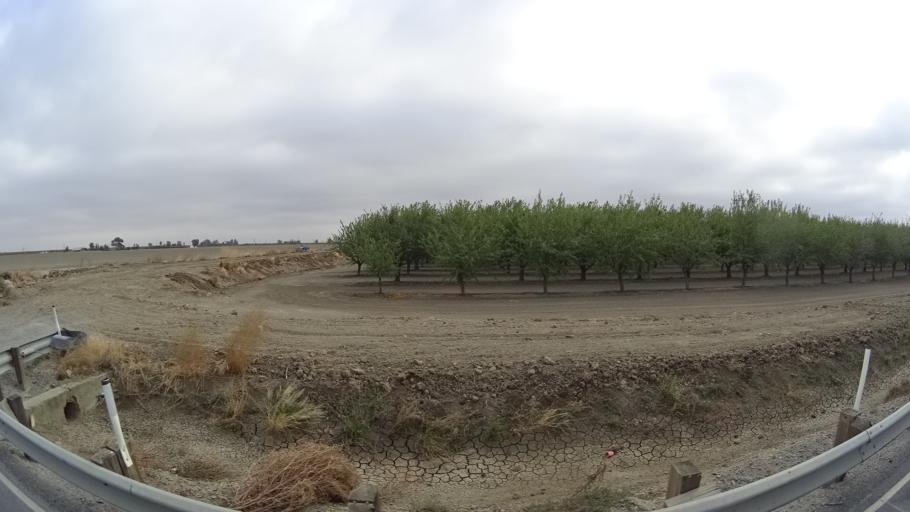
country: US
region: California
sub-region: Yolo County
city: Esparto
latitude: 38.7332
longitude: -122.0059
